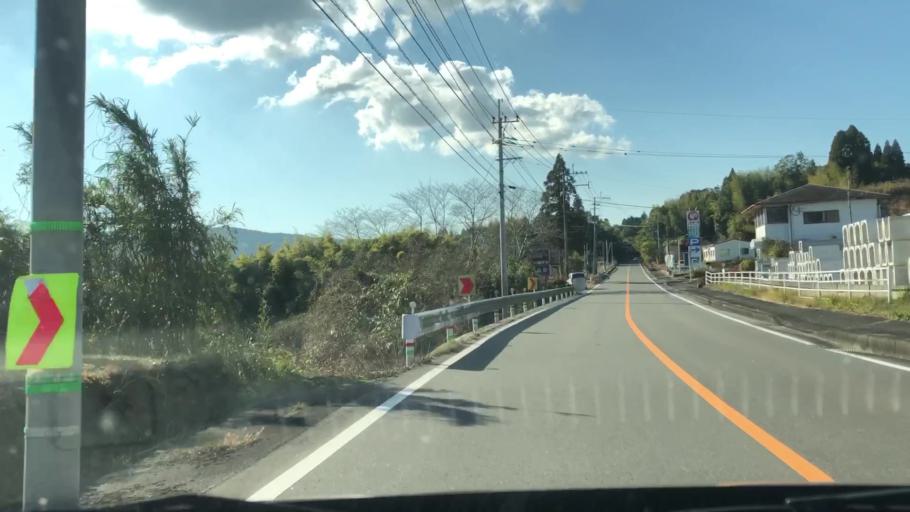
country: JP
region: Kagoshima
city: Satsumasendai
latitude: 31.8585
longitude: 130.3686
